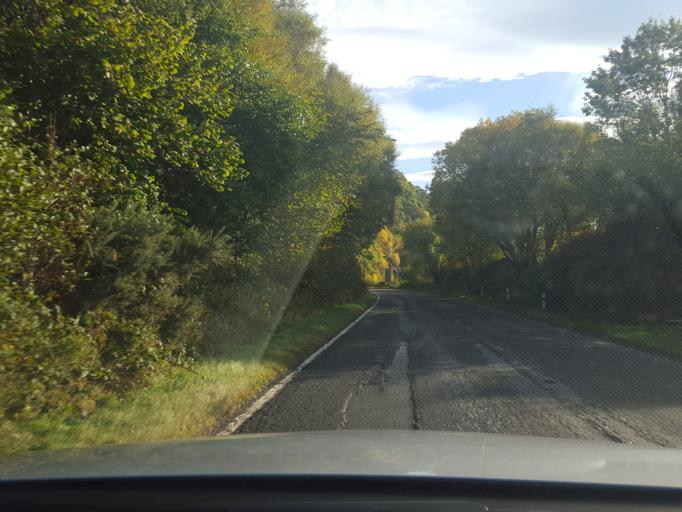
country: GB
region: Scotland
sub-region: Highland
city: Fort William
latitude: 57.2621
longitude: -5.4975
